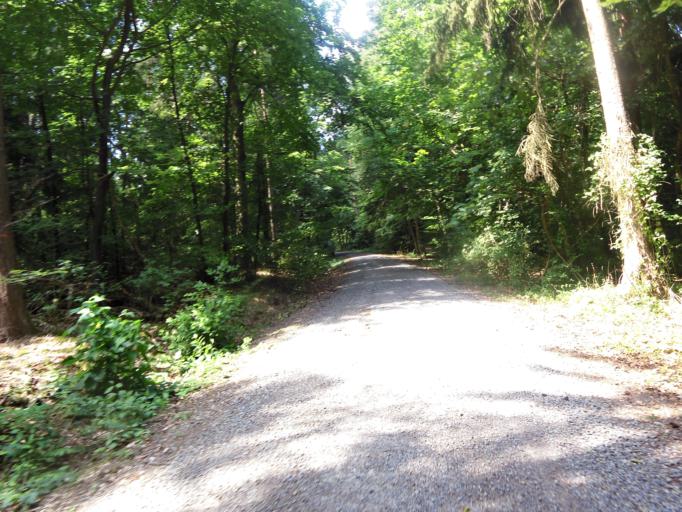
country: DE
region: Bavaria
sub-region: Regierungsbezirk Unterfranken
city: Gadheim
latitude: 49.8211
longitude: 9.9130
